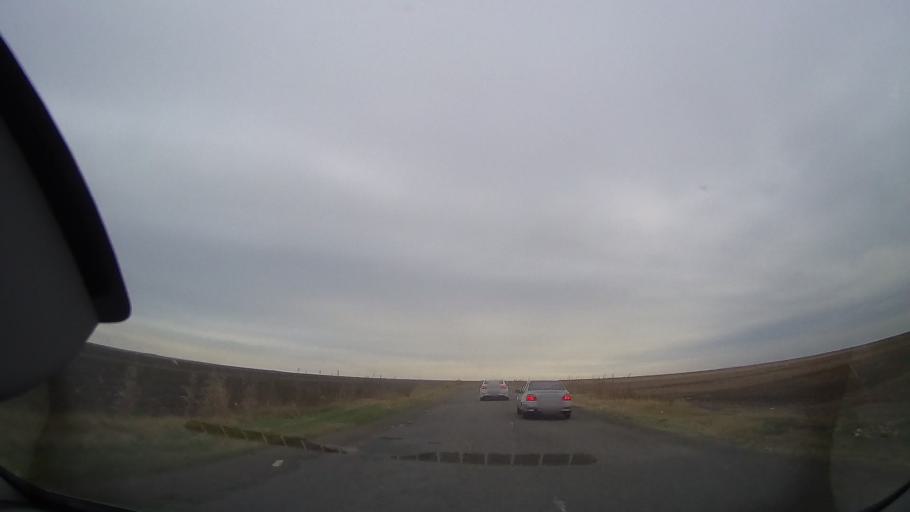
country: RO
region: Ialomita
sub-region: Oras Amara
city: Amara
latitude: 44.6665
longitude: 27.3008
